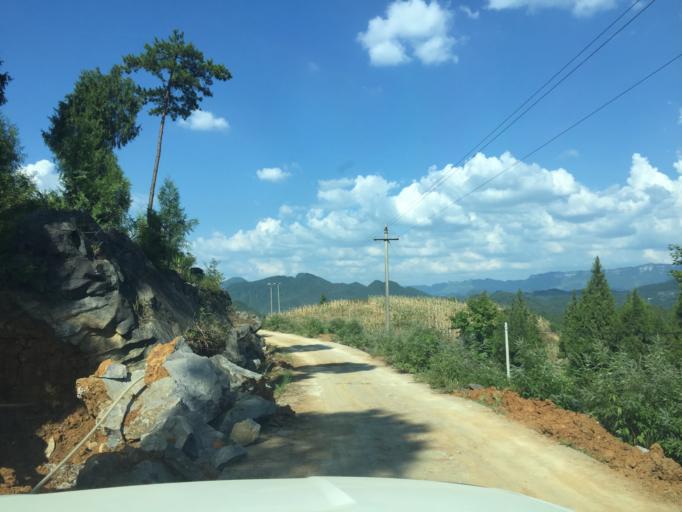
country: CN
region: Guizhou Sheng
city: Jiashi
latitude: 28.3357
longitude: 108.3091
